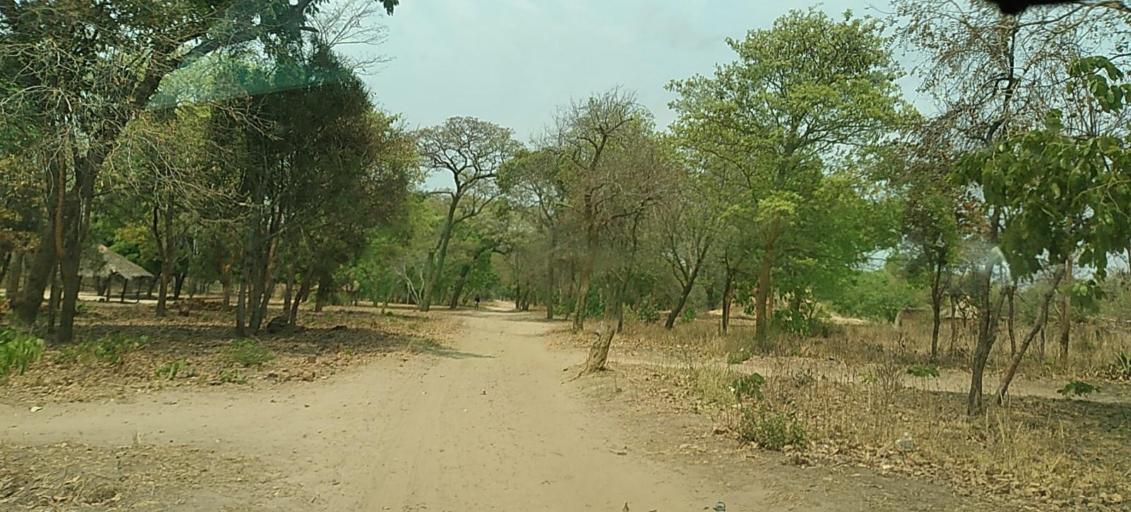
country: ZM
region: North-Western
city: Kabompo
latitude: -13.5581
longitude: 24.4468
